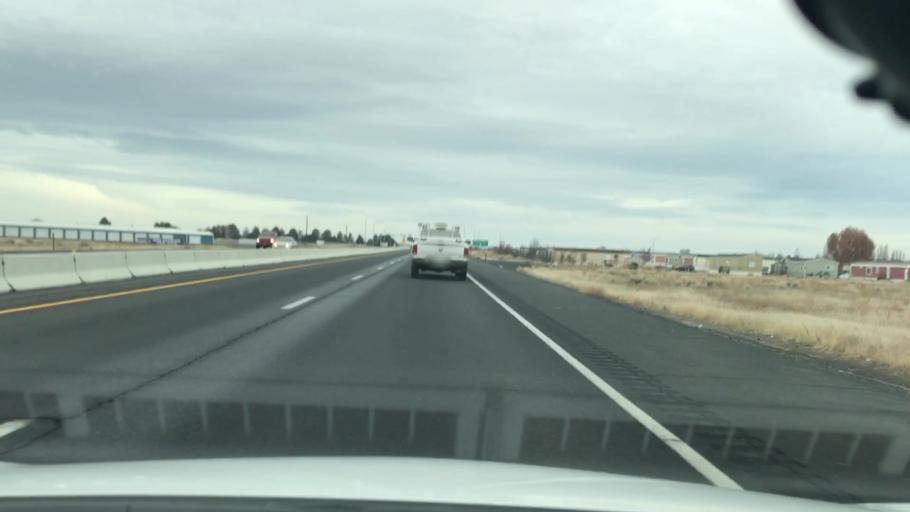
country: US
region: Washington
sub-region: Grant County
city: Cascade Valley
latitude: 47.1547
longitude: -119.3068
